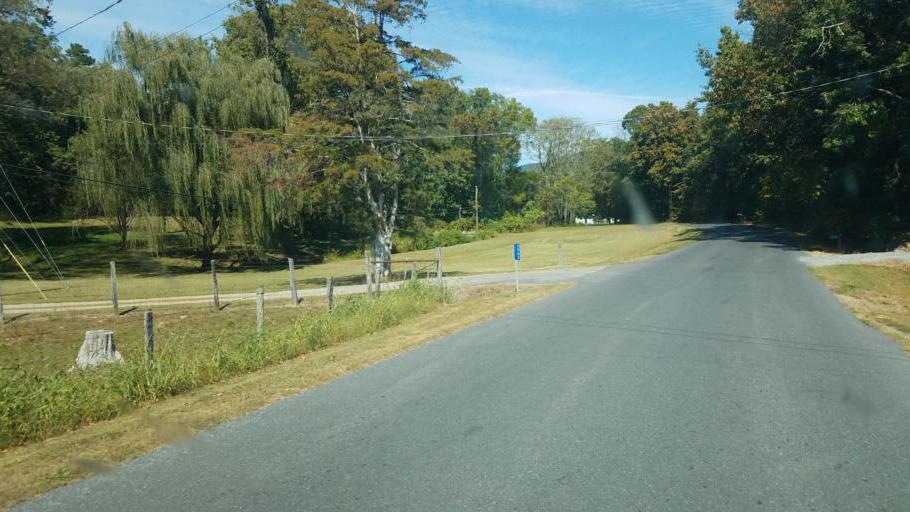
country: US
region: Virginia
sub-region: Rockingham County
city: Elkton
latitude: 38.4373
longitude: -78.5659
